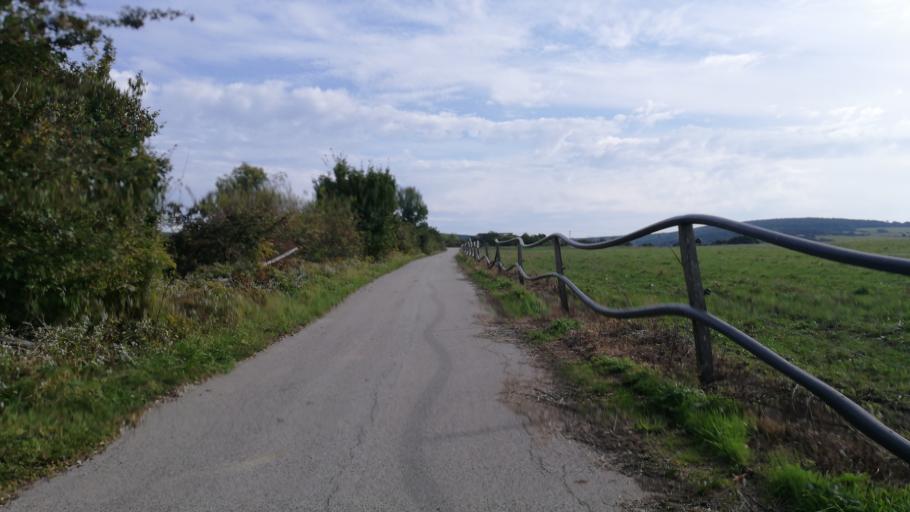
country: CZ
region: South Moravian
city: Sudomerice
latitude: 48.8407
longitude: 17.2835
